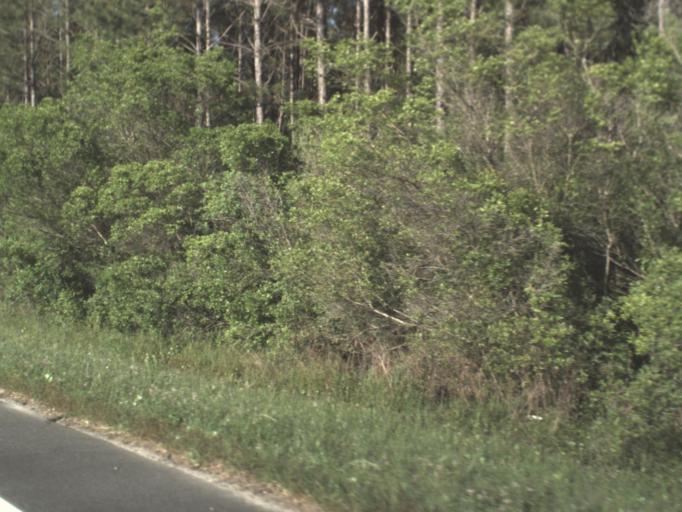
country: US
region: Florida
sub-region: Liberty County
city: Bristol
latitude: 30.3454
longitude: -84.8205
